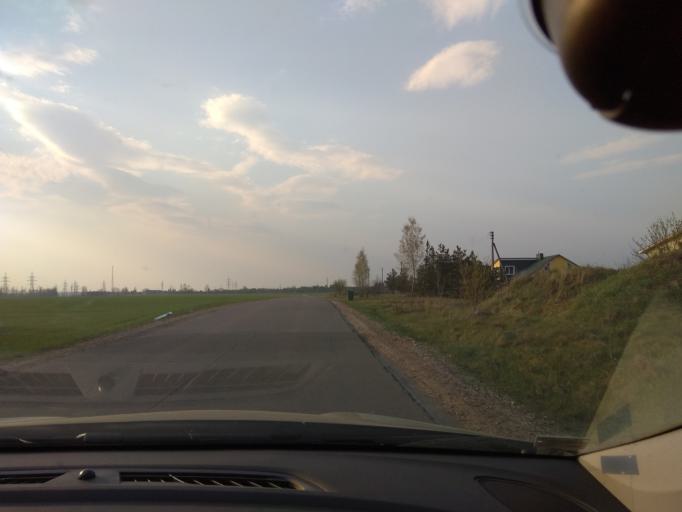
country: LT
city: Baltoji Voke
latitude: 54.6061
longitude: 25.1317
